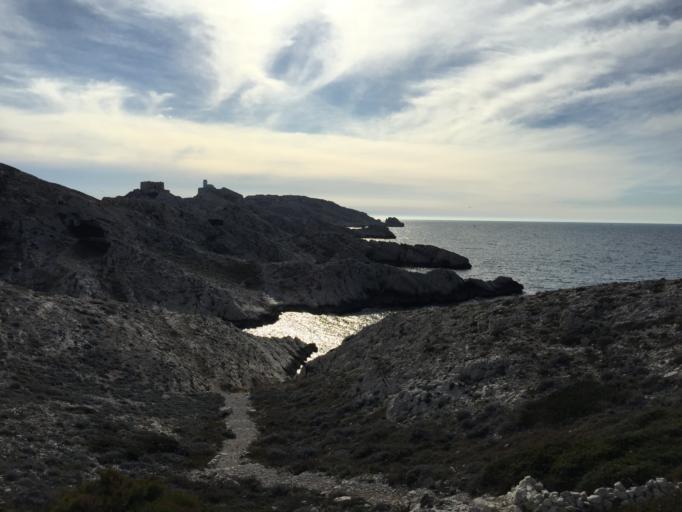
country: FR
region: Provence-Alpes-Cote d'Azur
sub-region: Departement des Bouches-du-Rhone
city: Marseille 07
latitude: 43.2752
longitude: 5.3032
